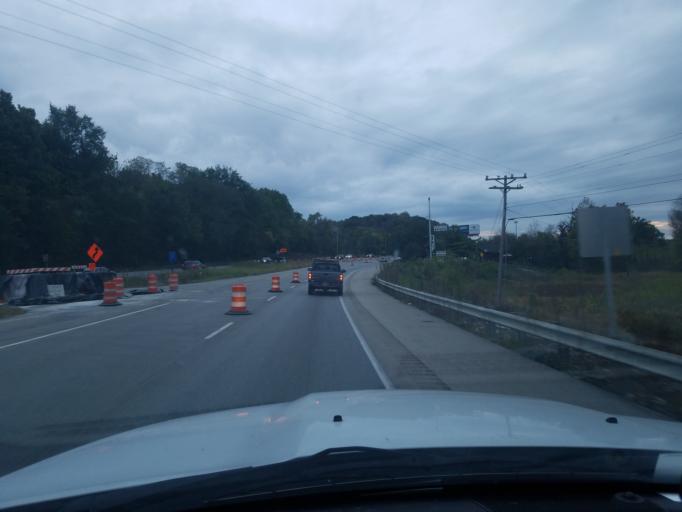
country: US
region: Kentucky
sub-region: Henderson County
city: Henderson
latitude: 37.8896
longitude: -87.5570
